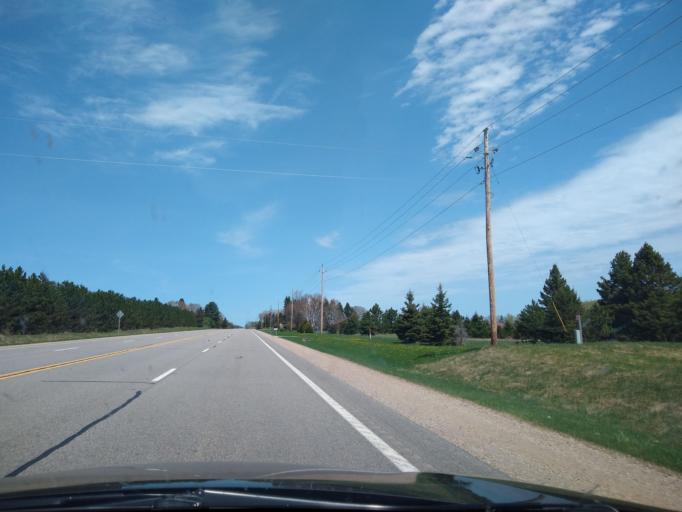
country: US
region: Michigan
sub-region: Delta County
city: Gladstone
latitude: 46.0815
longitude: -86.9808
